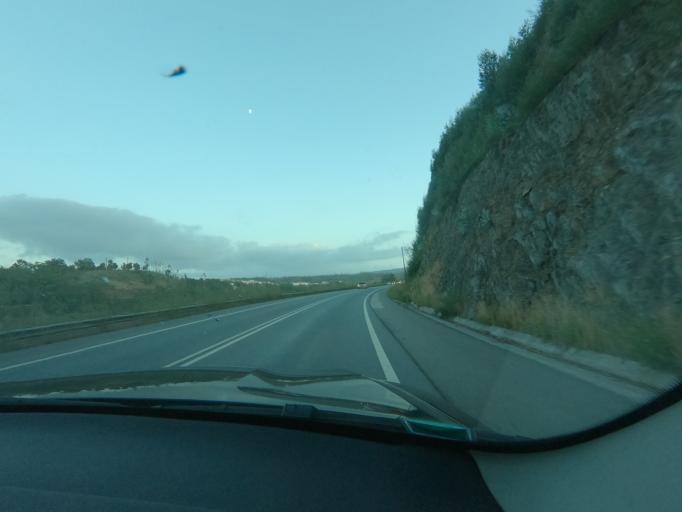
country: PT
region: Viseu
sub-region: Mortagua
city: Mortagua
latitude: 40.3308
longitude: -8.2287
